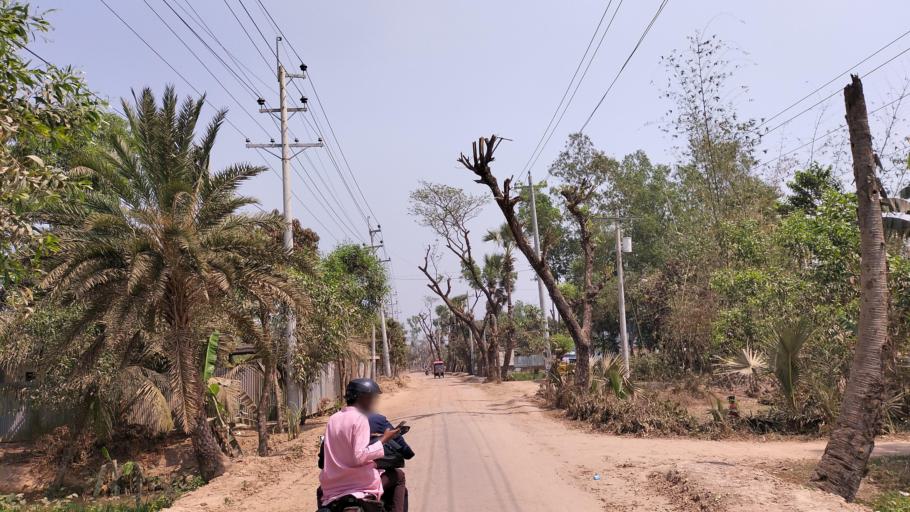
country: BD
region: Dhaka
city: Sakhipur
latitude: 24.3061
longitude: 90.3146
